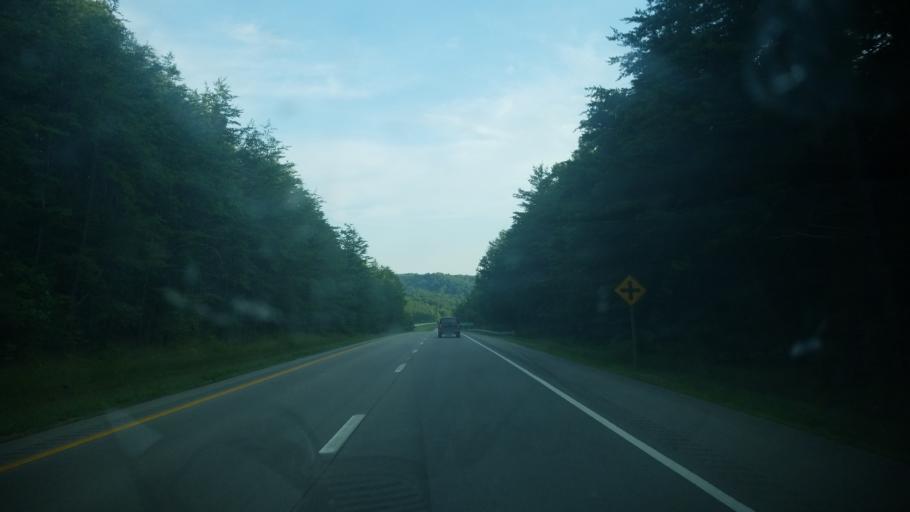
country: US
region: Ohio
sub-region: Adams County
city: Peebles
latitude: 39.0123
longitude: -83.2964
